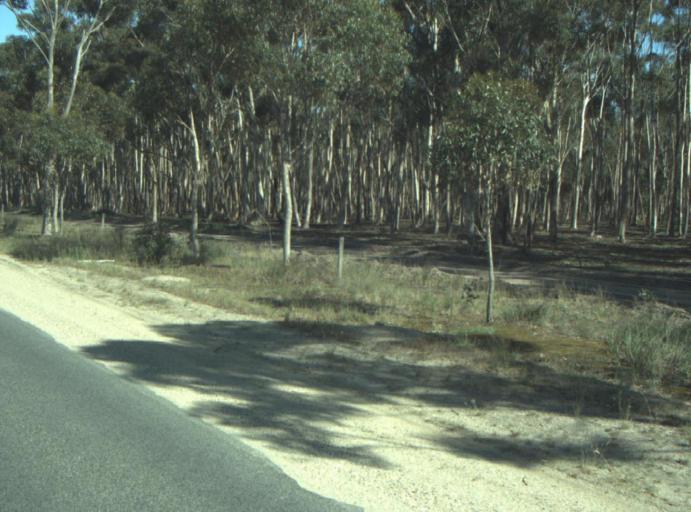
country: AU
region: Victoria
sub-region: Greater Geelong
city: Lara
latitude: -37.9665
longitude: 144.4163
